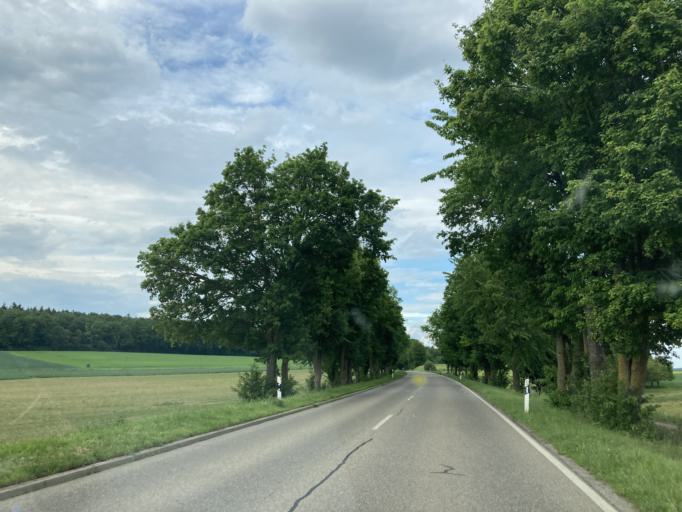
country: DE
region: Baden-Wuerttemberg
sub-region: Karlsruhe Region
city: Knittlingen
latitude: 49.0401
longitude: 8.7403
